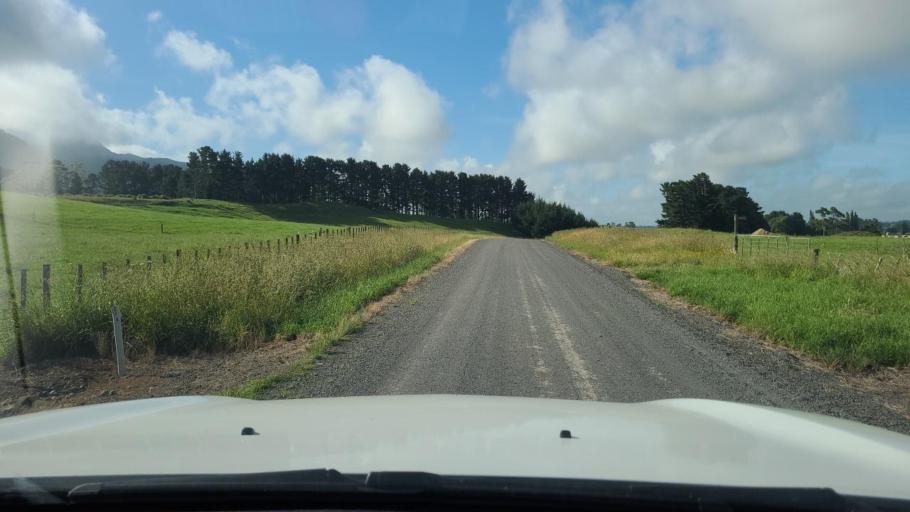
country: NZ
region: Bay of Plenty
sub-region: Western Bay of Plenty District
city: Katikati
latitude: -37.6062
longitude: 175.7971
